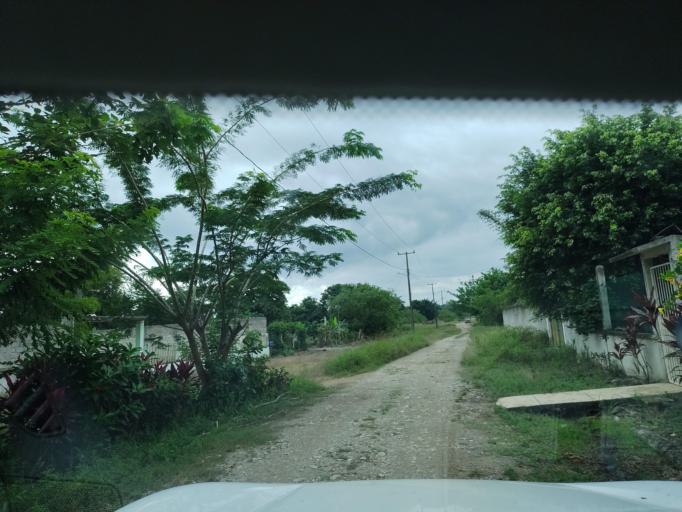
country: MX
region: Veracruz
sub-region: Atzalan
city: Colonias Pedernales
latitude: 20.0393
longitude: -97.0735
